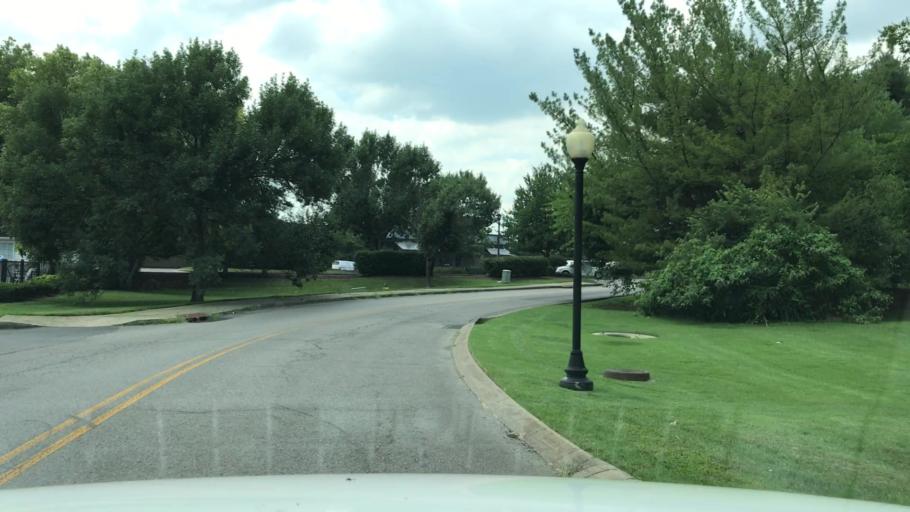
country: US
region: Tennessee
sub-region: Sumner County
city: Gallatin
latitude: 36.3789
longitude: -86.4711
